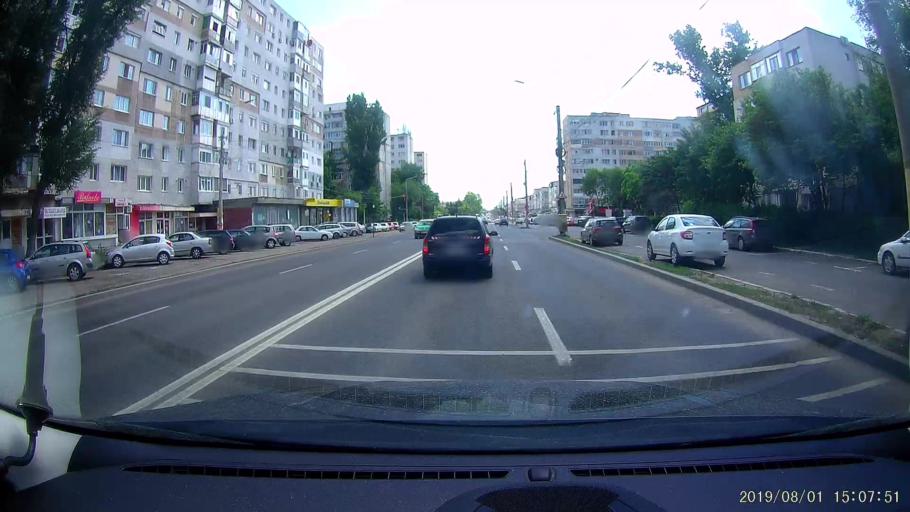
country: RO
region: Braila
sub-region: Municipiul Braila
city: Braila
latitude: 45.2452
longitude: 27.9489
